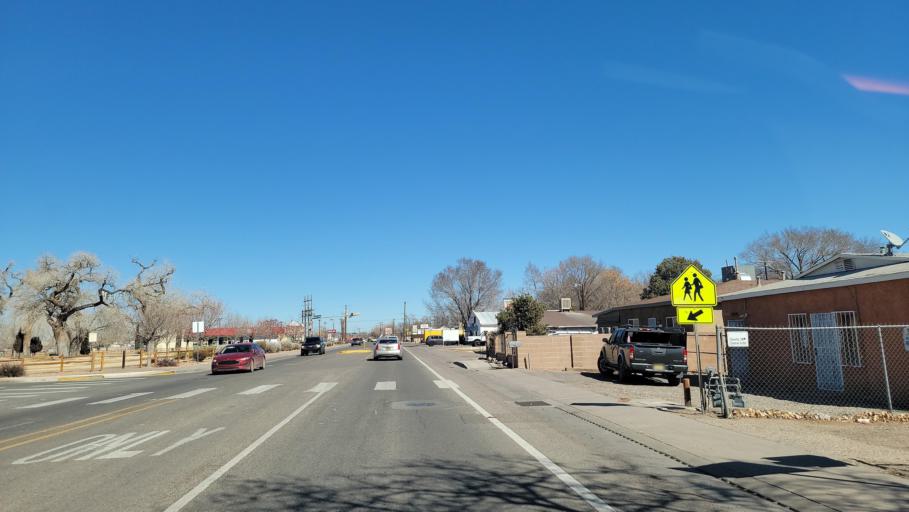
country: US
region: New Mexico
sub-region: Bernalillo County
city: South Valley
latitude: 35.0227
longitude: -106.6818
